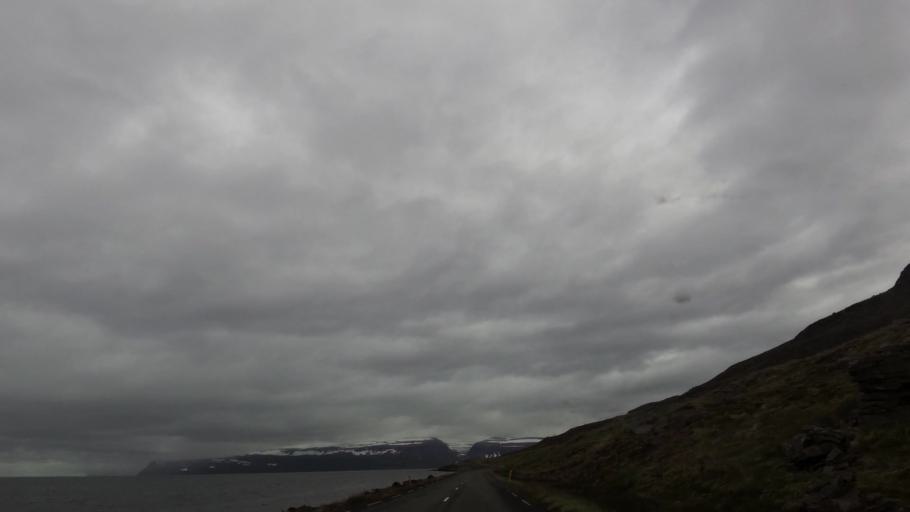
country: IS
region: Westfjords
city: Isafjoerdur
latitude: 66.0369
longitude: -22.7733
